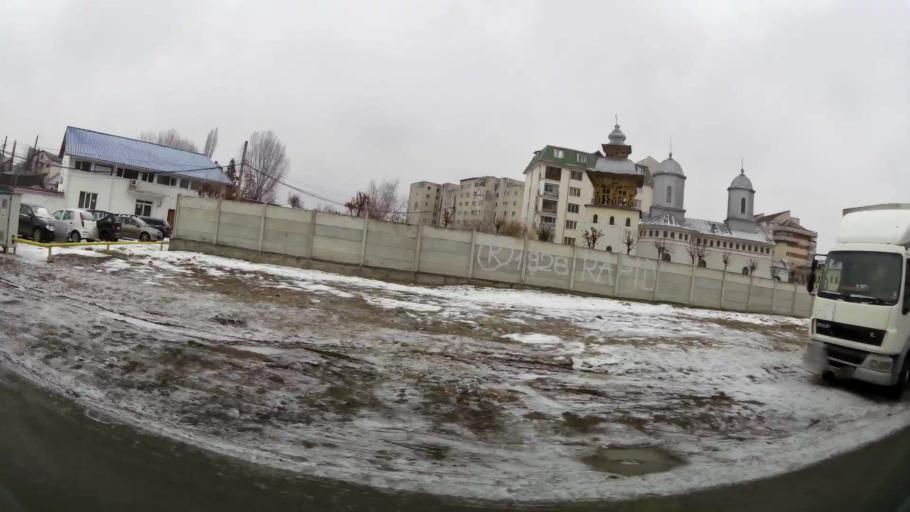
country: RO
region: Dambovita
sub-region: Municipiul Targoviste
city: Targoviste
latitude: 44.9185
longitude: 25.4804
